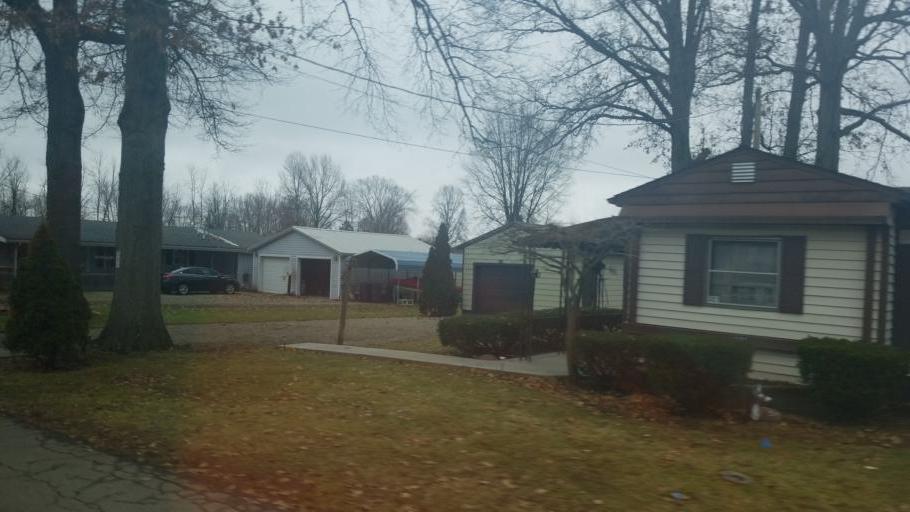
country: US
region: Ohio
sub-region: Crawford County
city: Galion
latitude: 40.7281
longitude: -82.7673
